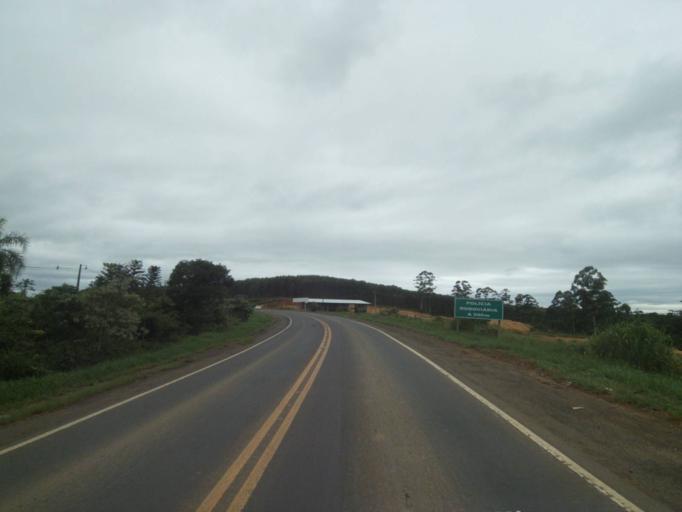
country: BR
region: Parana
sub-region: Telemaco Borba
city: Telemaco Borba
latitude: -24.3873
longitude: -50.6853
